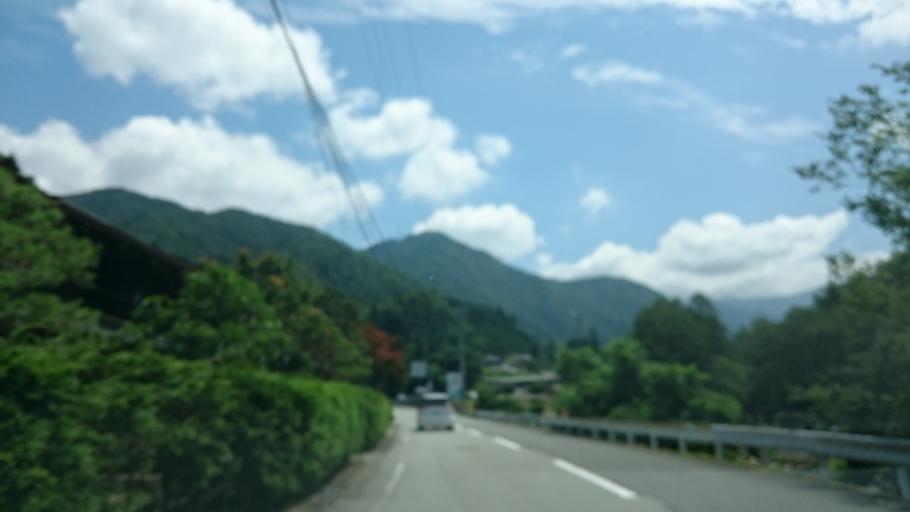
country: JP
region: Gifu
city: Takayama
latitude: 35.9255
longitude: 137.3129
